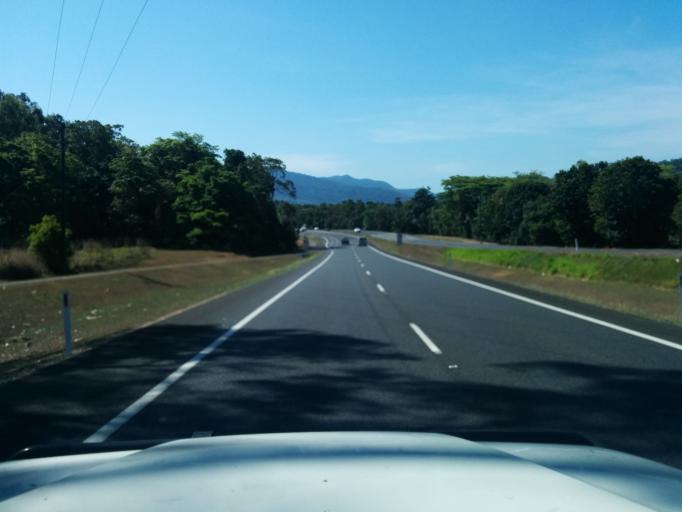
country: AU
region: Queensland
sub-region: Cairns
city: Redlynch
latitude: -16.9082
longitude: 145.7120
